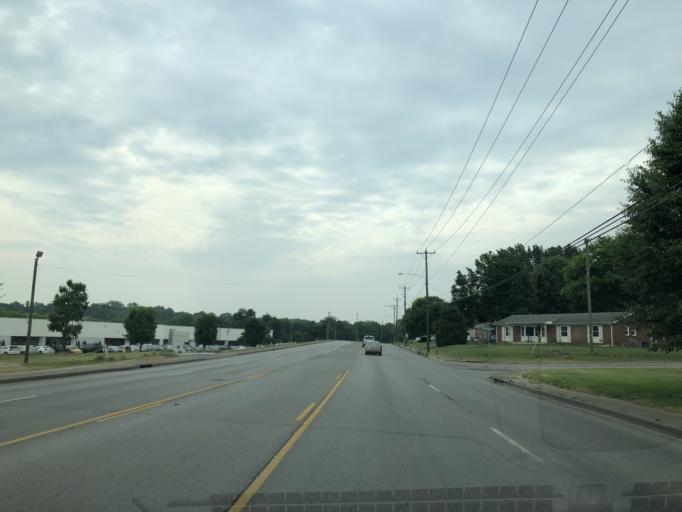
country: US
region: Tennessee
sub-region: Davidson County
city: Oak Hill
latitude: 36.0795
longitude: -86.6847
